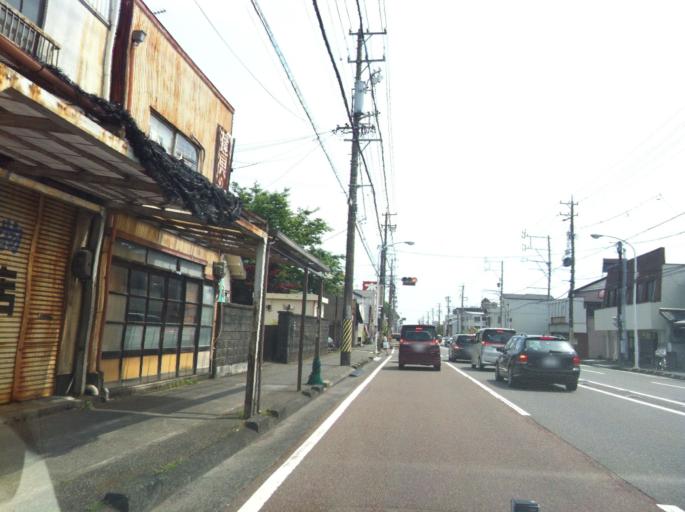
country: JP
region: Shizuoka
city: Shizuoka-shi
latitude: 34.9937
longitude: 138.3702
